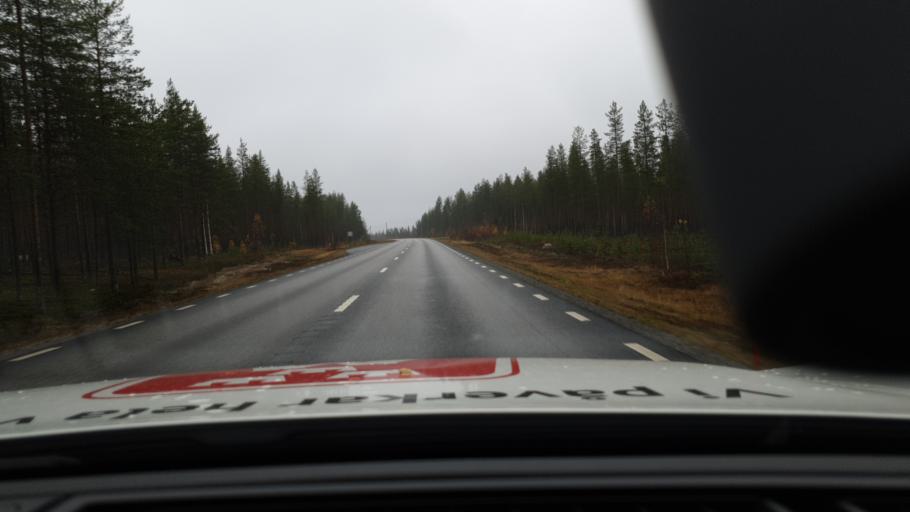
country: SE
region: Norrbotten
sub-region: Overkalix Kommun
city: OEverkalix
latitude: 66.6185
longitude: 22.2328
